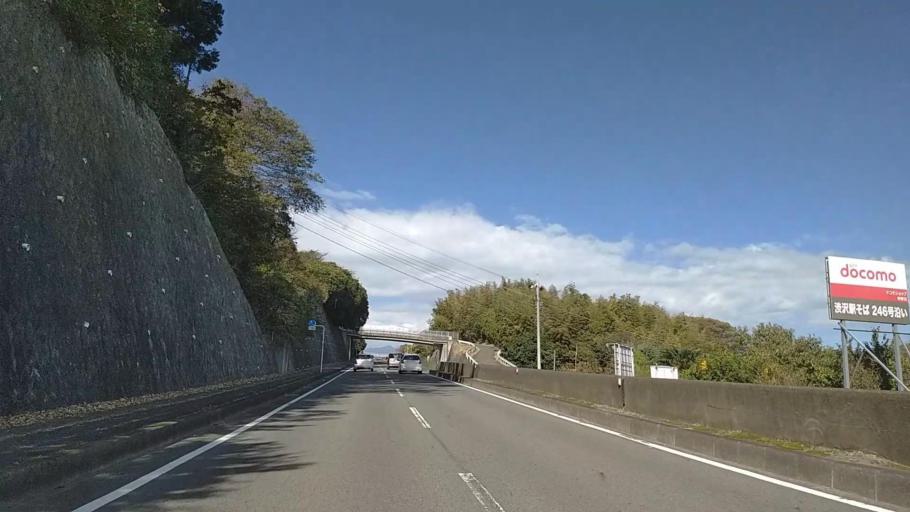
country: JP
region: Kanagawa
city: Ninomiya
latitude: 35.3188
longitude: 139.2405
